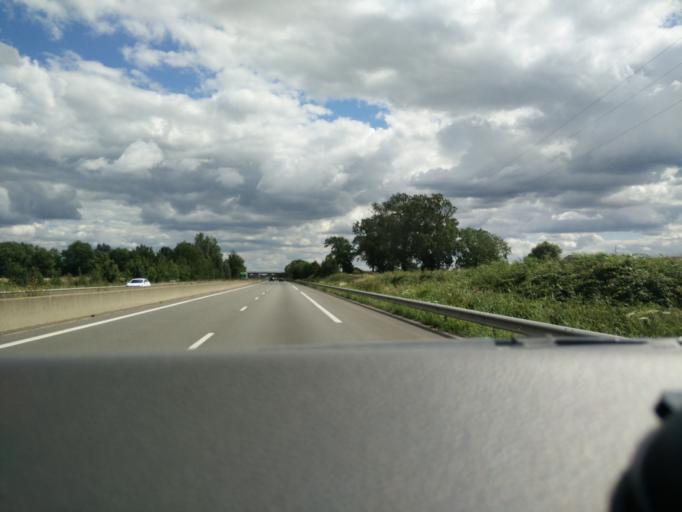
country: FR
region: Nord-Pas-de-Calais
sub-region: Departement du Nord
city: Herzeele
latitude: 50.8706
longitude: 2.5295
